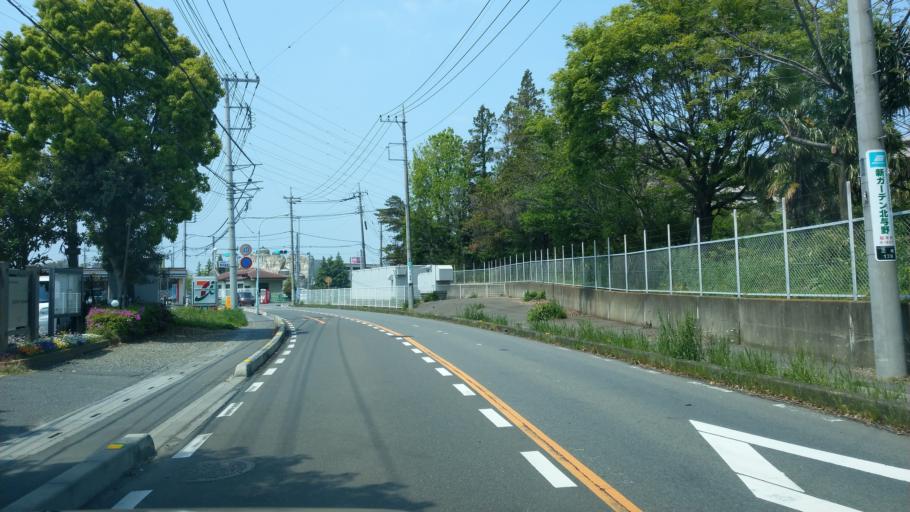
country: JP
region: Saitama
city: Yono
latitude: 35.9148
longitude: 139.5987
